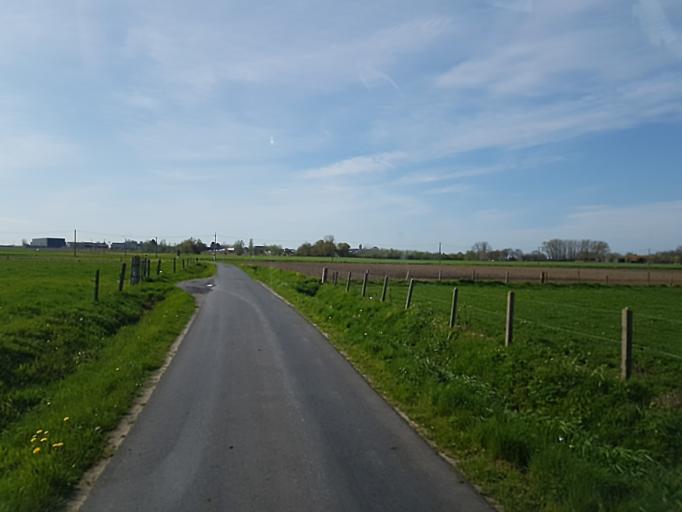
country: BE
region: Flanders
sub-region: Provincie West-Vlaanderen
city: Waregem
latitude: 50.8520
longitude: 3.4274
